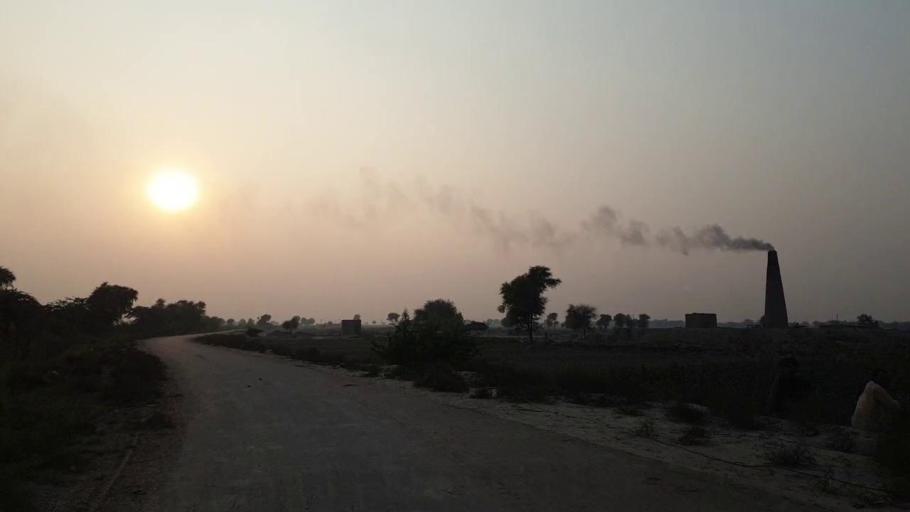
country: PK
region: Sindh
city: Bhan
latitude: 26.5320
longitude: 67.7042
